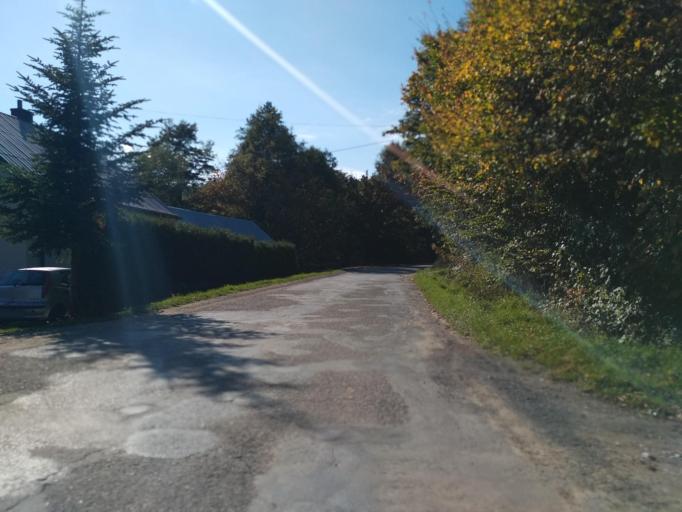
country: PL
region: Subcarpathian Voivodeship
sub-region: Powiat debicki
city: Slotowa
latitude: 49.9419
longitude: 21.2836
